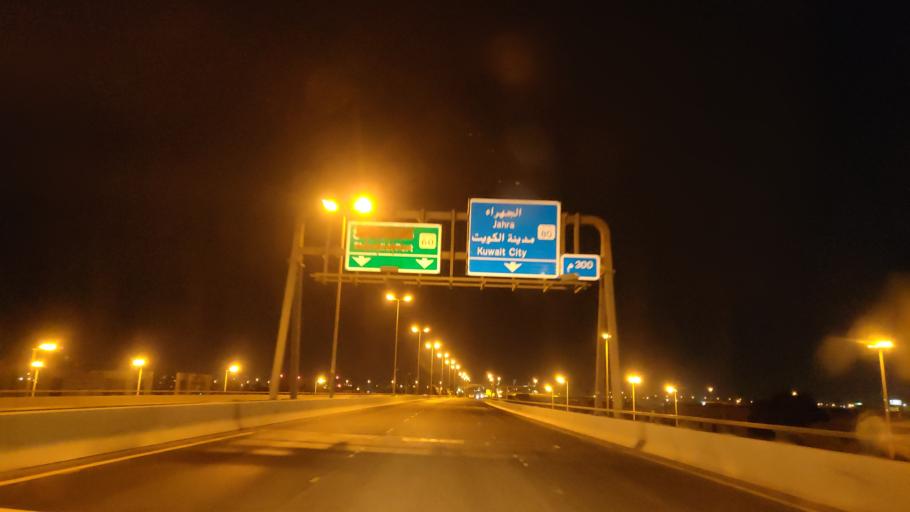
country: KW
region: Al Asimah
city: Ar Rabiyah
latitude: 29.3230
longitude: 47.9367
